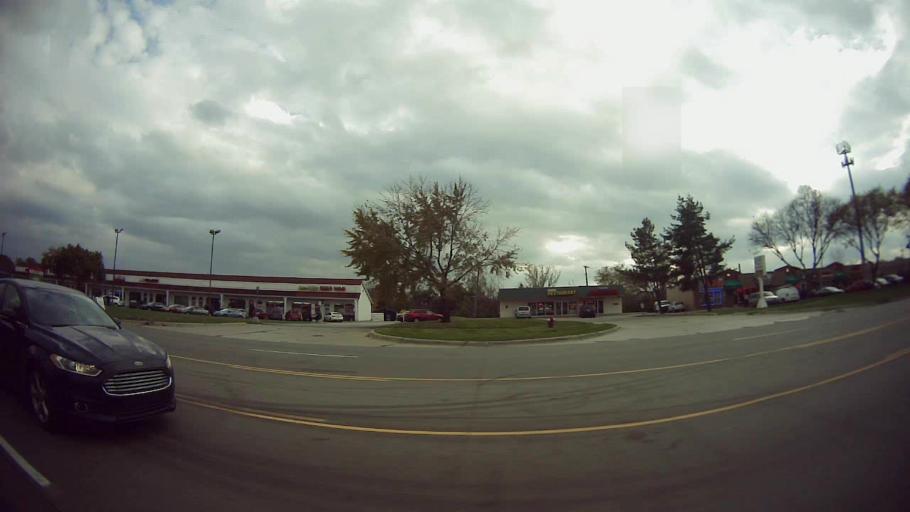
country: US
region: Michigan
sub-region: Macomb County
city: Sterling Heights
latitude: 42.5502
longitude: -83.0674
